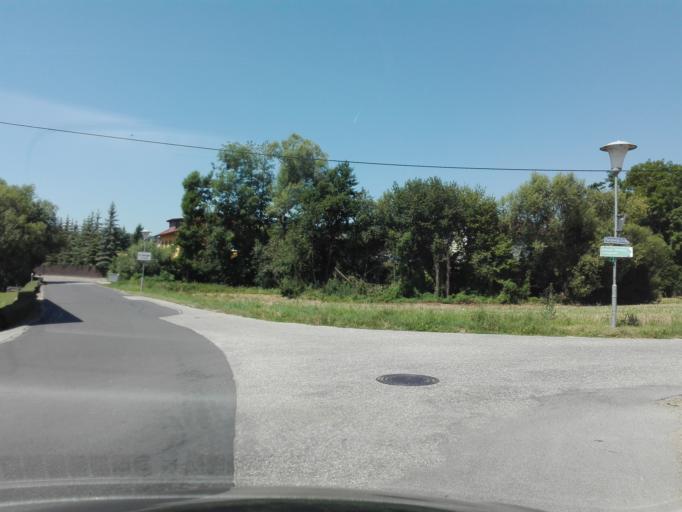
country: AT
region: Upper Austria
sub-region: Politischer Bezirk Urfahr-Umgebung
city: Engerwitzdorf
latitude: 48.2828
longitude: 14.4459
